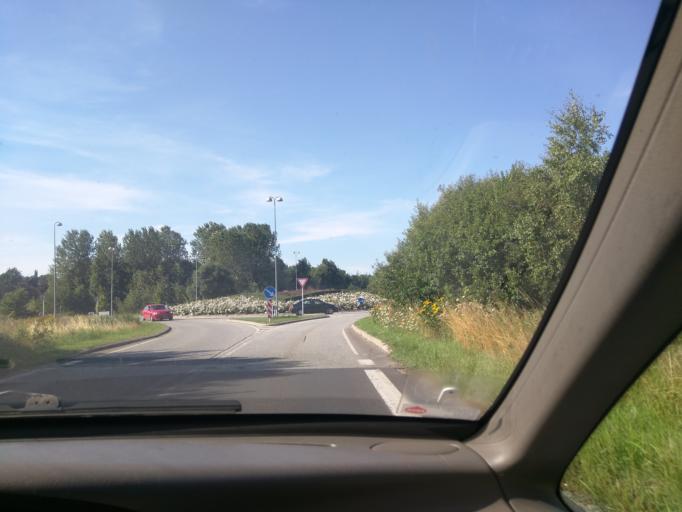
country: DK
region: Central Jutland
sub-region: Viborg Kommune
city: Bjerringbro
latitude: 56.3851
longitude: 9.6735
